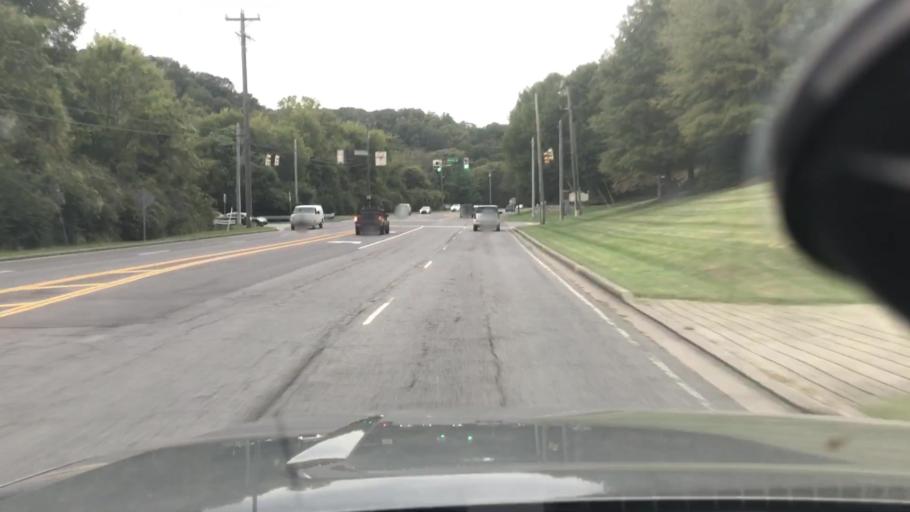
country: US
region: Tennessee
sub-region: Davidson County
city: Belle Meade
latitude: 36.0624
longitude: -86.9166
